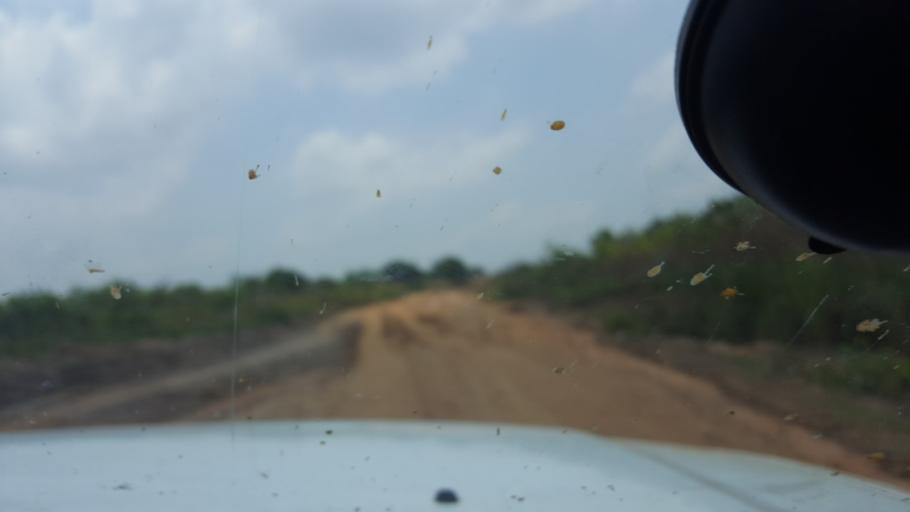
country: CD
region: Bandundu
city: Mushie
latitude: -3.7492
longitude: 16.6611
